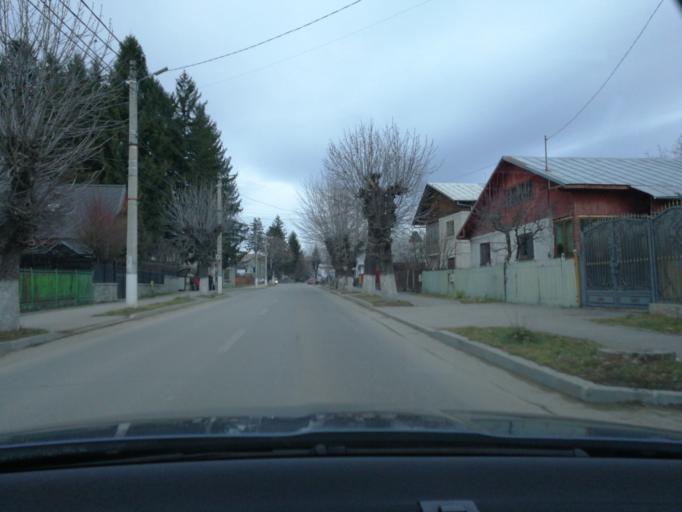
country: RO
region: Prahova
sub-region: Oras Breaza
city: Breaza de Jos
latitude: 45.1737
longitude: 25.6723
